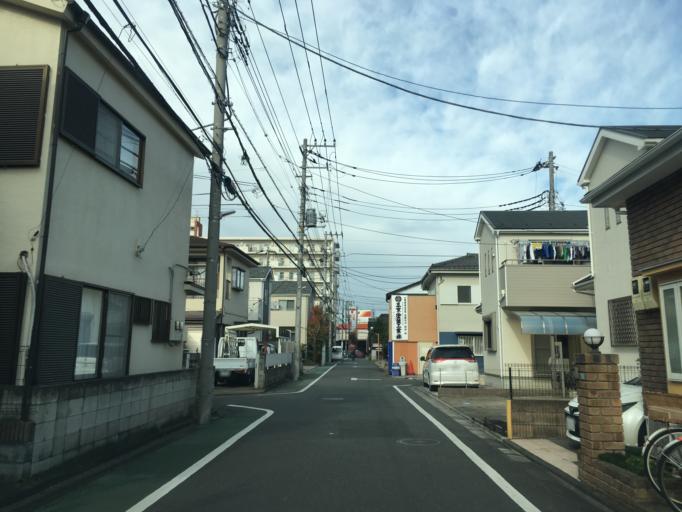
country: JP
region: Tokyo
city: Tanashicho
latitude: 35.7385
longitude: 139.5068
